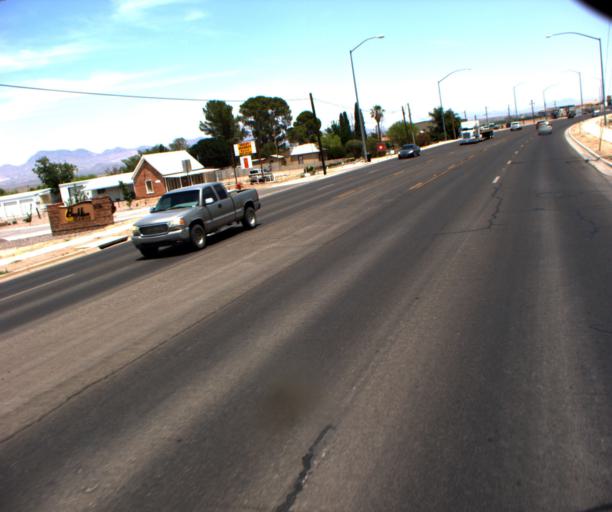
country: US
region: Arizona
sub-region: Graham County
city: Thatcher
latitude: 32.8491
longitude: -109.7531
